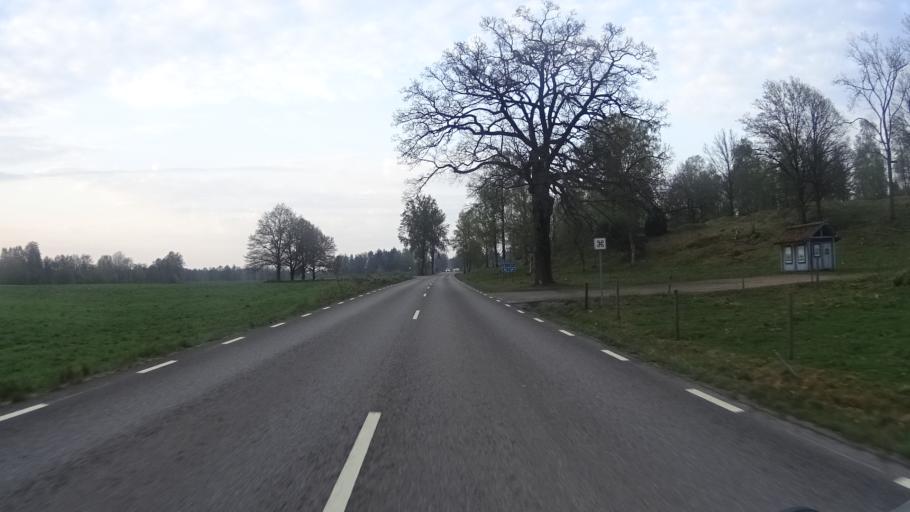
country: SE
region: Kronoberg
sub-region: Ljungby Kommun
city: Ljungby
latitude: 56.8466
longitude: 13.9742
